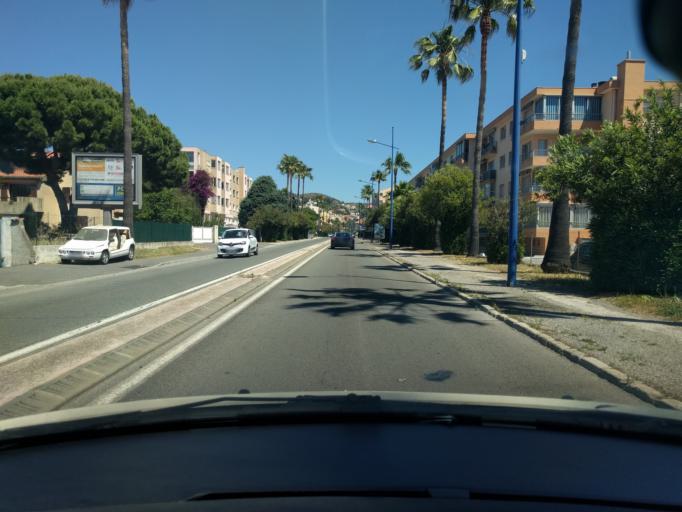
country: FR
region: Provence-Alpes-Cote d'Azur
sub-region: Departement du Var
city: Hyeres
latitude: 43.1097
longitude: 6.1288
